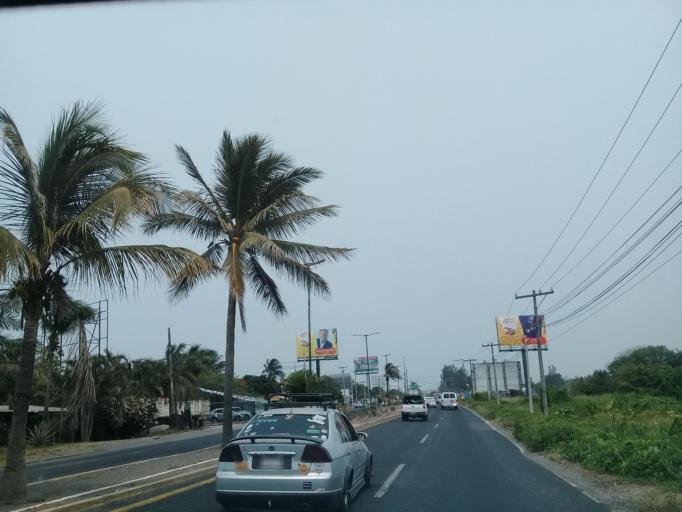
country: MX
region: Veracruz
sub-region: Veracruz
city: Hacienda Sotavento
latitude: 19.1446
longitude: -96.1615
